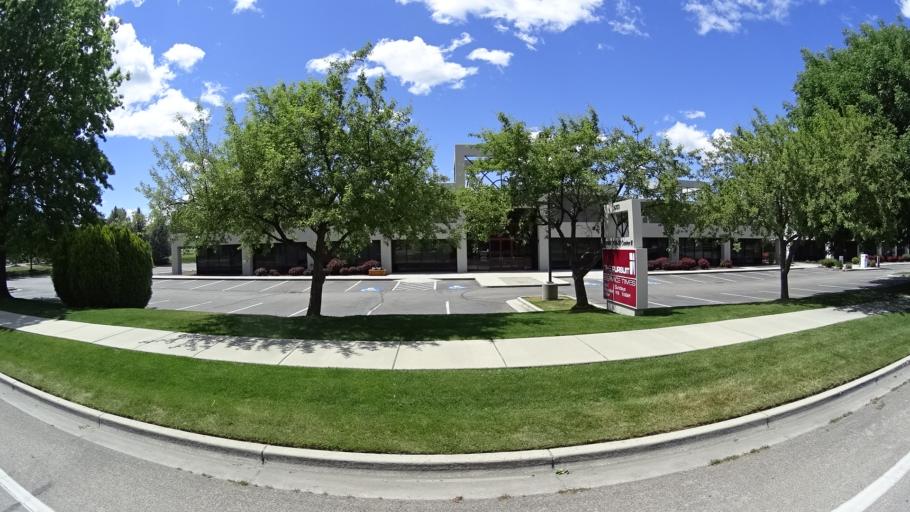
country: US
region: Idaho
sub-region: Ada County
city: Eagle
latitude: 43.6609
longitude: -116.3418
